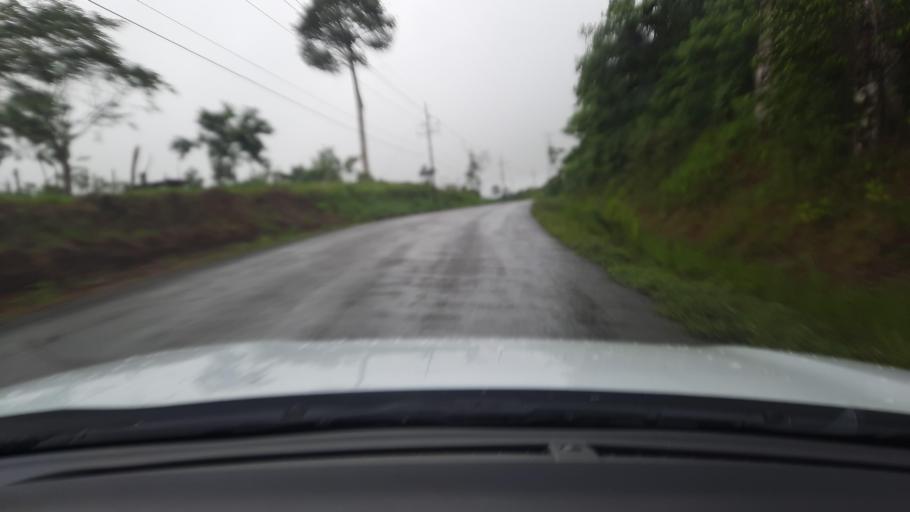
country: NI
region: Rivas
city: Cardenas
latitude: 11.0406
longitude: -85.3735
